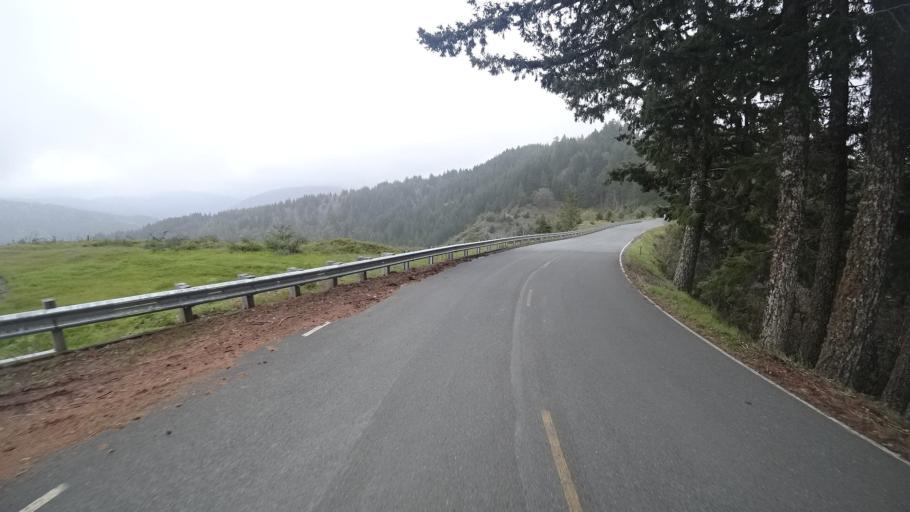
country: US
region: California
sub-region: Humboldt County
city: Westhaven-Moonstone
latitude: 41.1464
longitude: -123.8461
